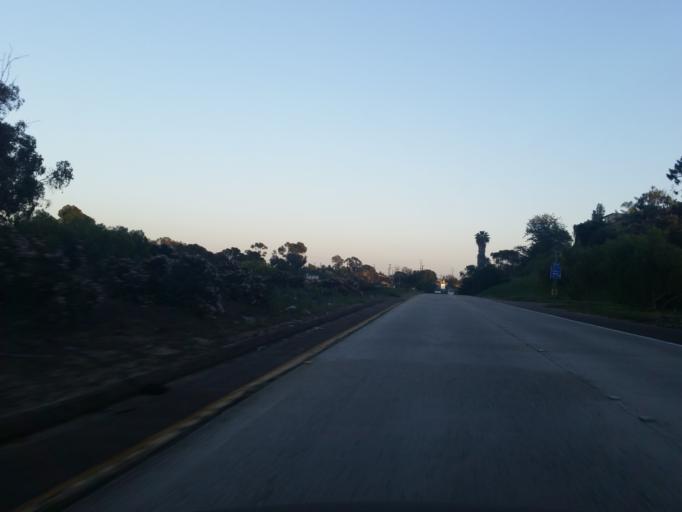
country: US
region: California
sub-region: San Diego County
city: San Diego
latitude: 32.7356
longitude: -117.1149
